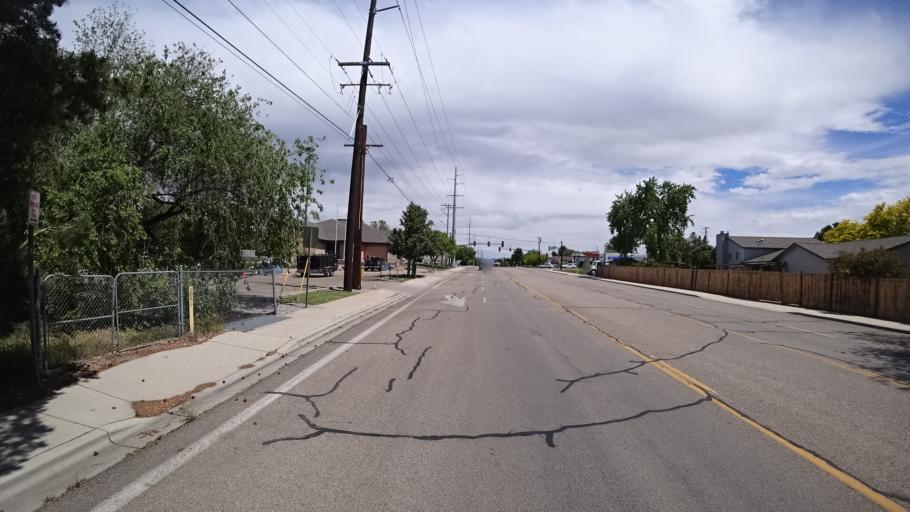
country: US
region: Idaho
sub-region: Ada County
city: Meridian
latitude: 43.5758
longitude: -116.3154
